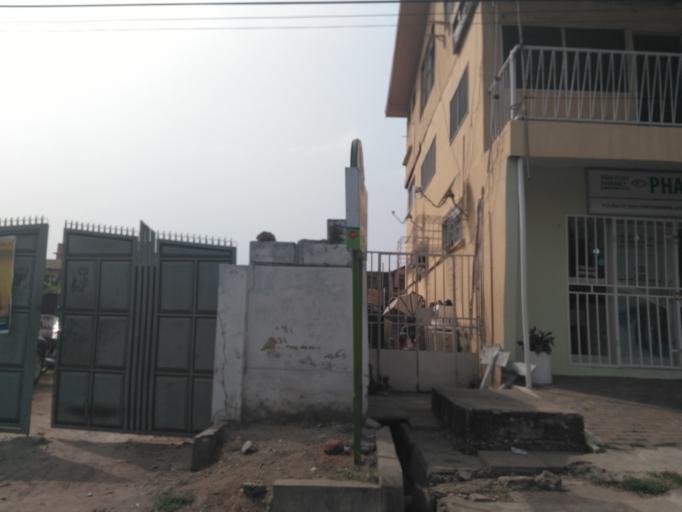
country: GH
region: Greater Accra
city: Accra
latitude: 5.5596
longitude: -0.1815
